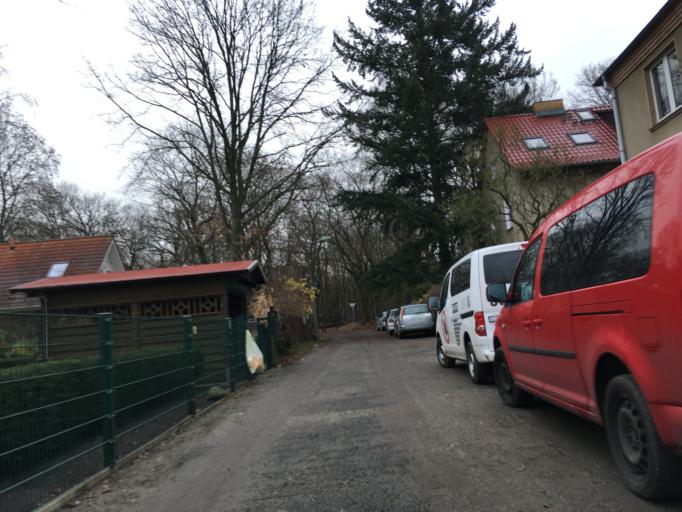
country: DE
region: Berlin
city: Wilhelmsruh
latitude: 52.5773
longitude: 13.3797
